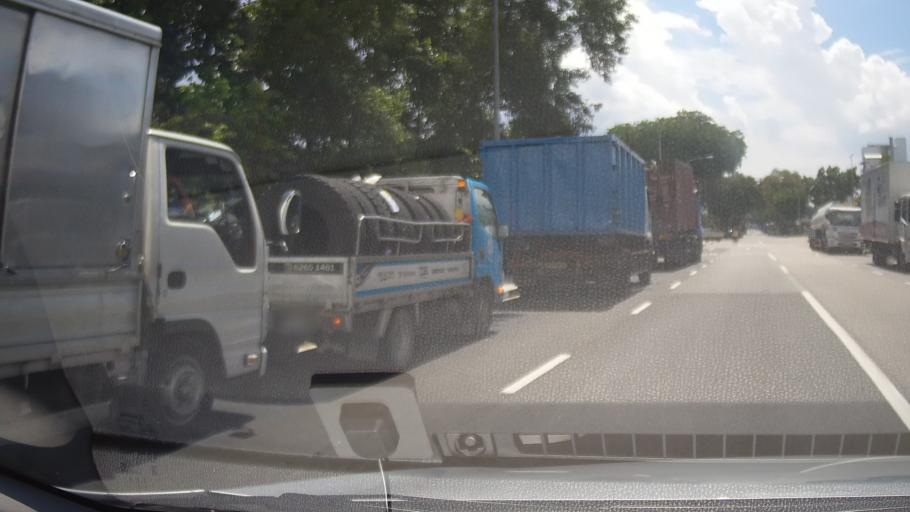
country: MY
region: Johor
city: Johor Bahru
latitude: 1.3299
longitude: 103.6941
